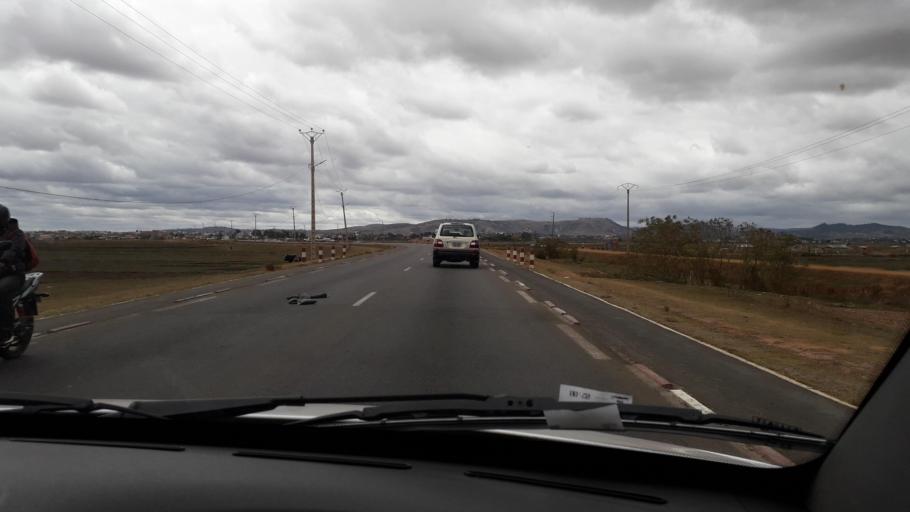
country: MG
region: Analamanga
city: Antananarivo
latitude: -18.8218
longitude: 47.5159
